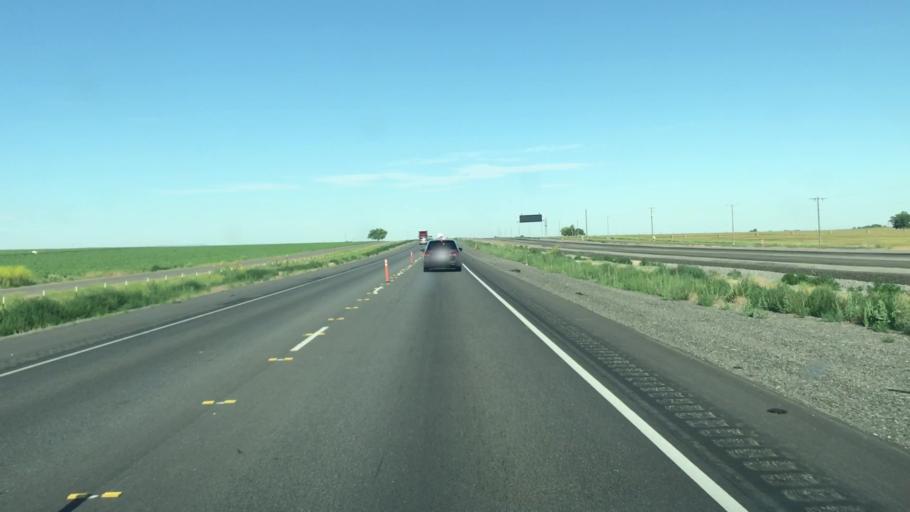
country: US
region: Idaho
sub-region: Twin Falls County
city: Hansen
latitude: 42.5762
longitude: -114.2585
